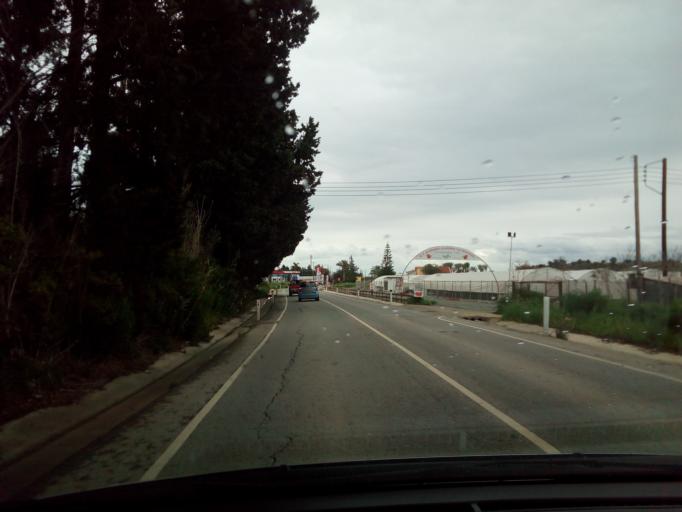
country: CY
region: Larnaka
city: Kofinou
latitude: 34.7434
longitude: 33.3242
